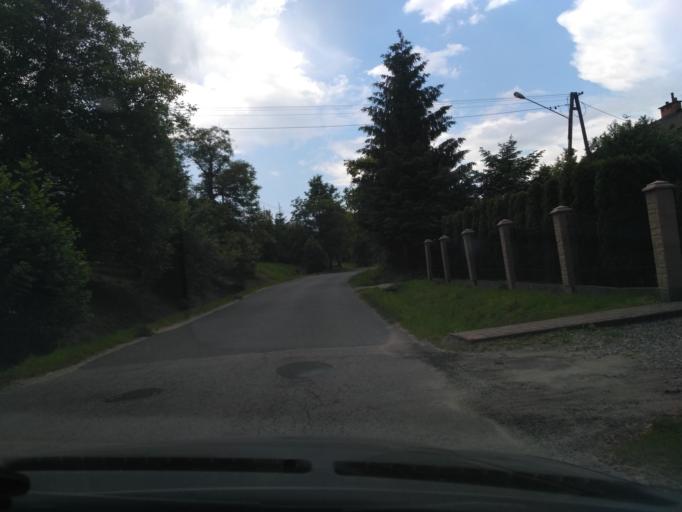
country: PL
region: Subcarpathian Voivodeship
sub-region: Powiat lancucki
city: Wysoka
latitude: 50.0354
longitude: 22.2374
